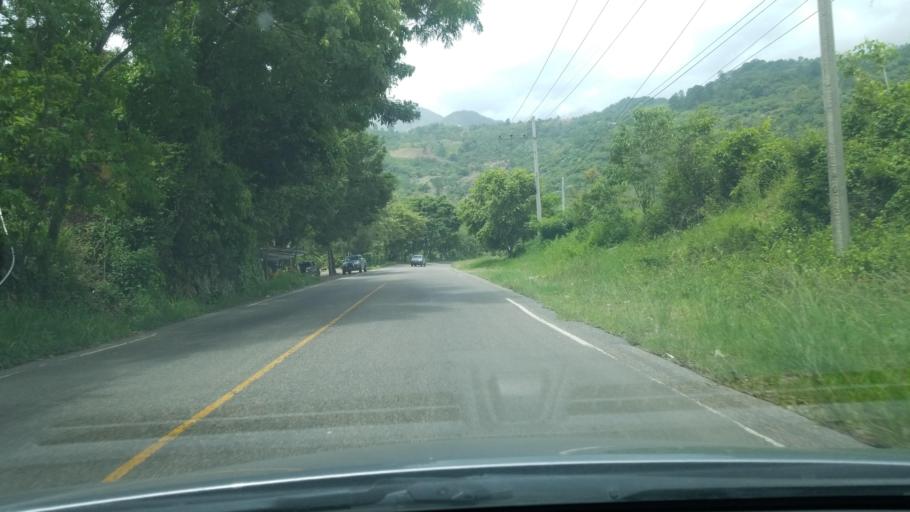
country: HN
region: Copan
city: Ojos de Agua
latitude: 14.6776
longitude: -88.8159
